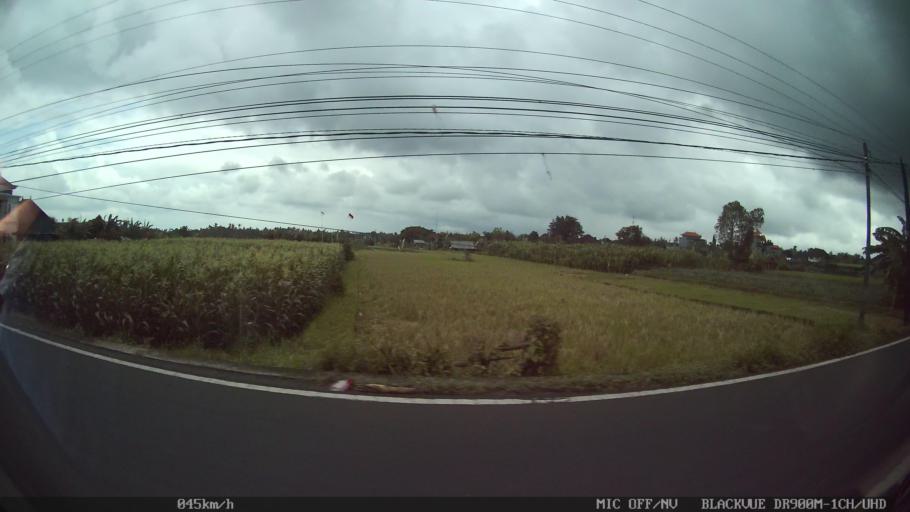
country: ID
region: Bali
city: Banjar Mambalkajanan
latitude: -8.5429
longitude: 115.2226
